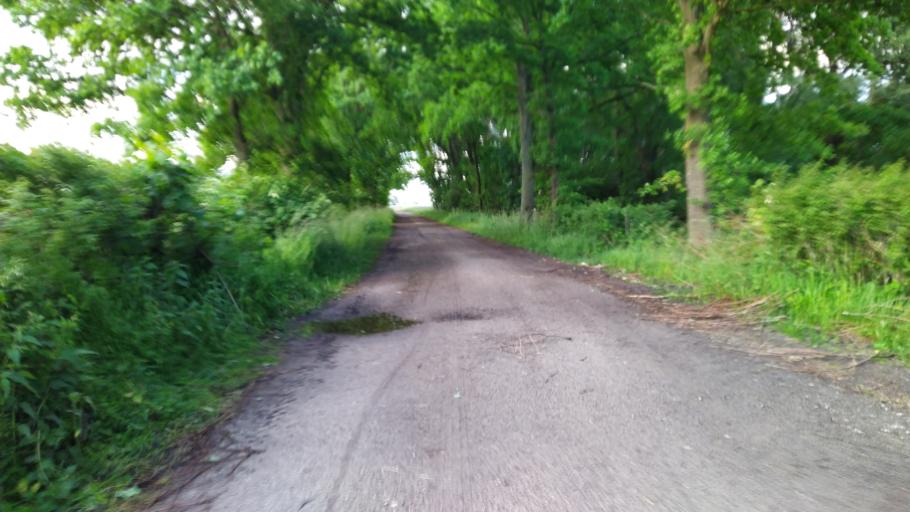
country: DE
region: Lower Saxony
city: Kutenholz
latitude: 53.4557
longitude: 9.3436
